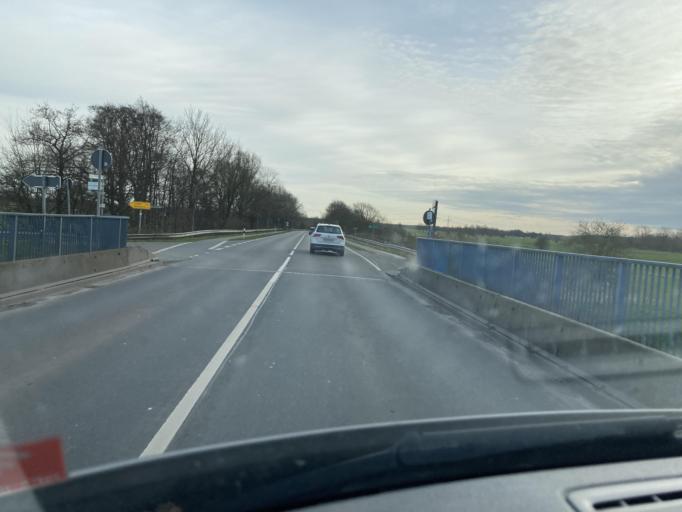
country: DE
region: Lower Saxony
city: Leer
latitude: 53.2199
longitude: 7.4838
